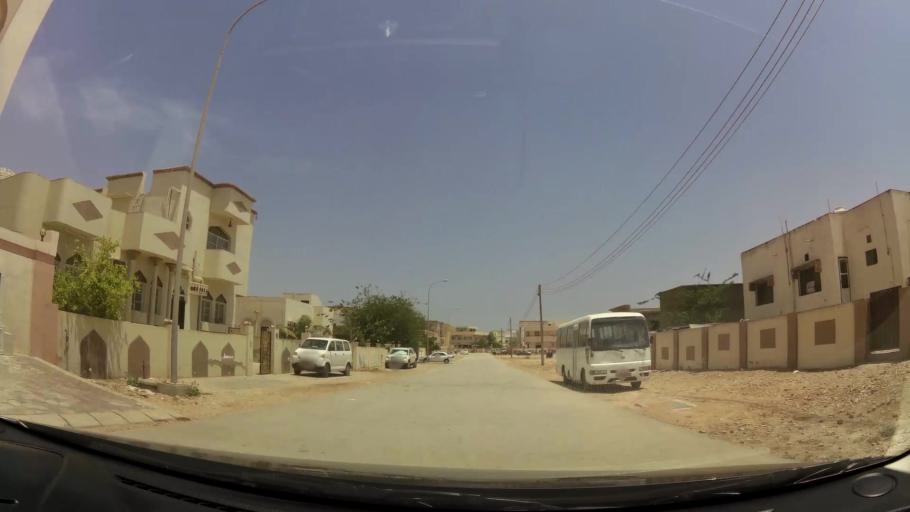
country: OM
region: Zufar
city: Salalah
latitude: 17.0765
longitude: 54.1491
